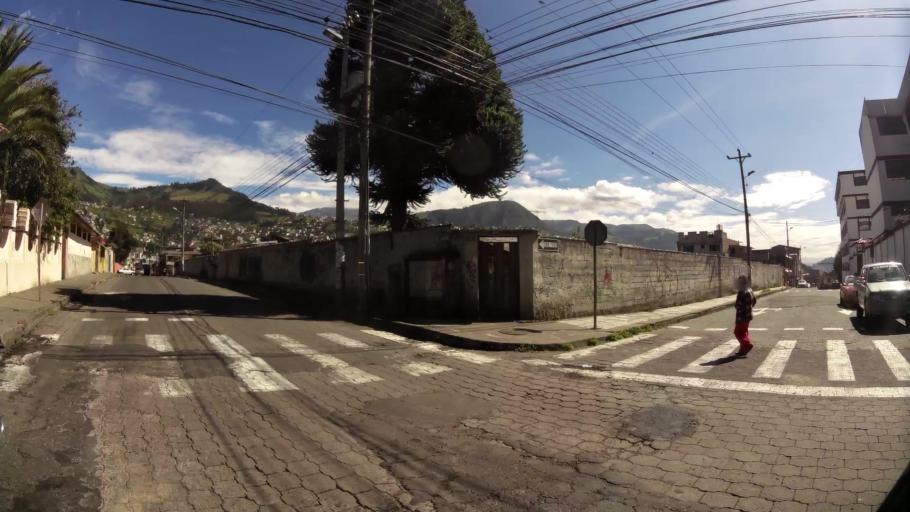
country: EC
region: Pichincha
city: Quito
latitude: -0.2754
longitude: -78.5541
